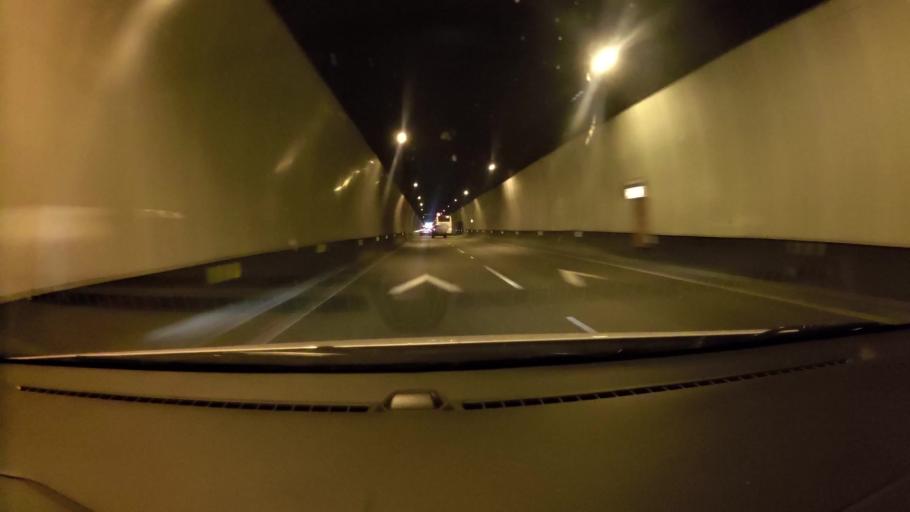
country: CL
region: Santiago Metropolitan
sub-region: Provincia de Melipilla
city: Melipilla
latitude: -33.3871
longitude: -71.2662
